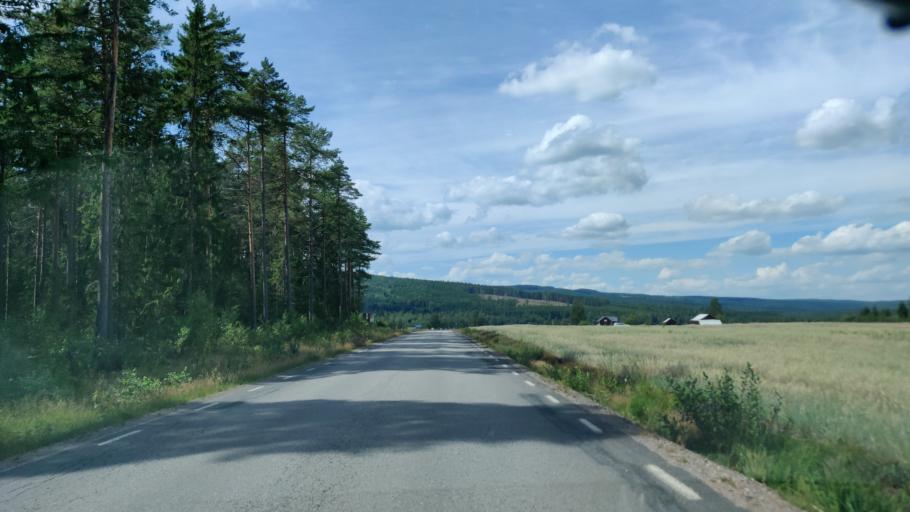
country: SE
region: Vaermland
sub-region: Hagfors Kommun
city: Ekshaerad
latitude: 60.0715
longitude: 13.4971
